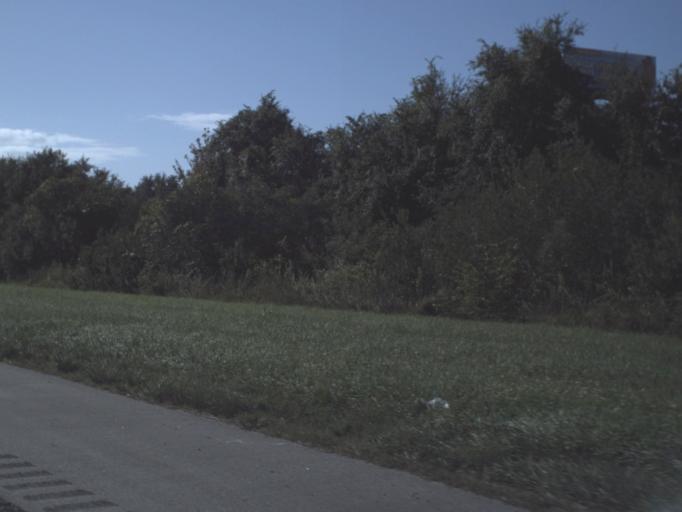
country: US
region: Florida
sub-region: Osceola County
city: Buenaventura Lakes
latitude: 28.2816
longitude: -81.3386
